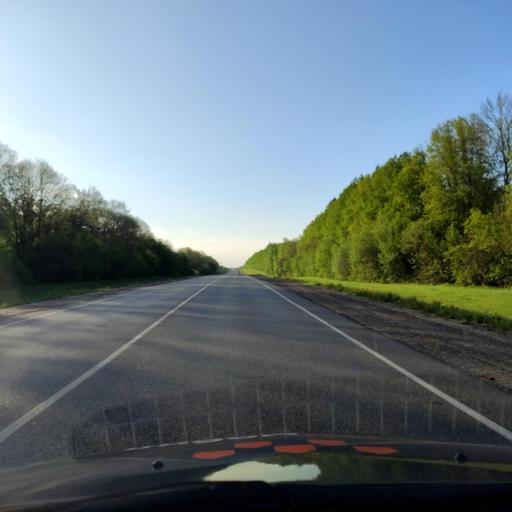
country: RU
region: Lipetsk
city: Yelets
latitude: 52.5715
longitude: 38.6589
